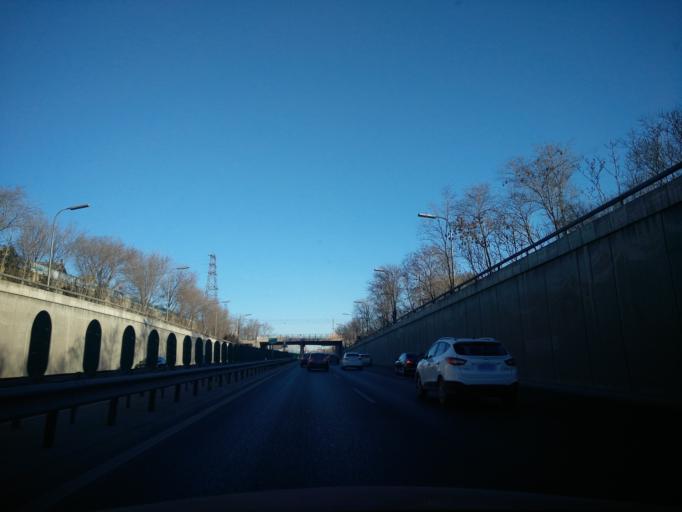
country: CN
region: Beijing
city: Lugu
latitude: 39.8506
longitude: 116.2151
